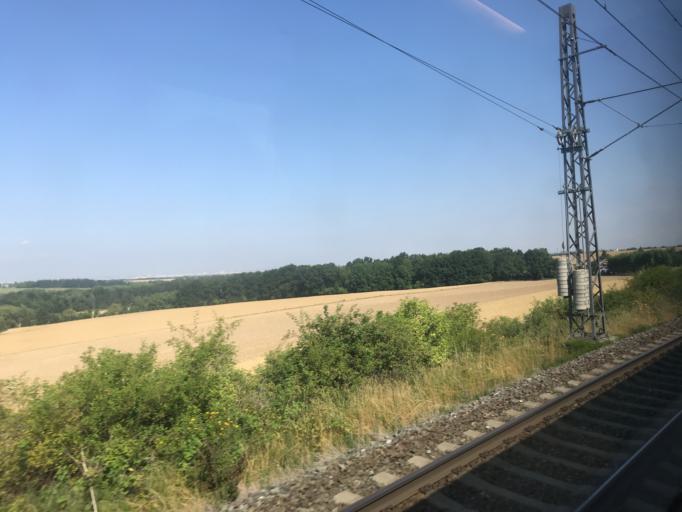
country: CZ
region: Central Bohemia
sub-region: Okres Praha-Vychod
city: Ricany
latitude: 49.9651
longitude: 14.6535
